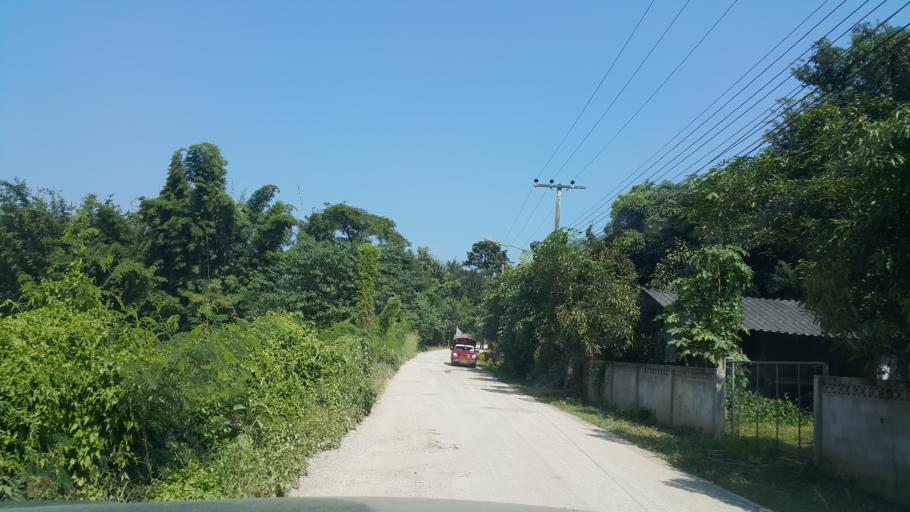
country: TH
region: Chiang Mai
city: Samoeng
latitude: 18.9085
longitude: 98.6011
